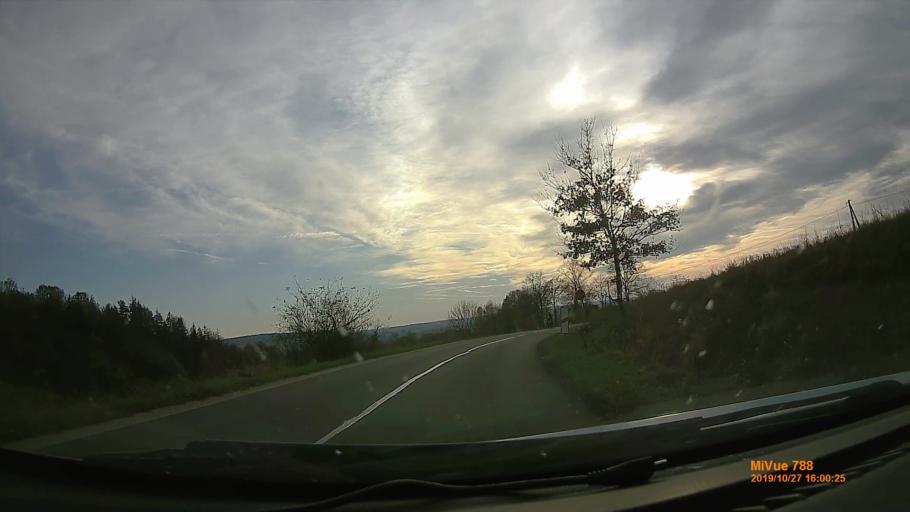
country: PL
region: Lower Silesian Voivodeship
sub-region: Powiat klodzki
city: Nowa Ruda
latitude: 50.5289
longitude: 16.5172
